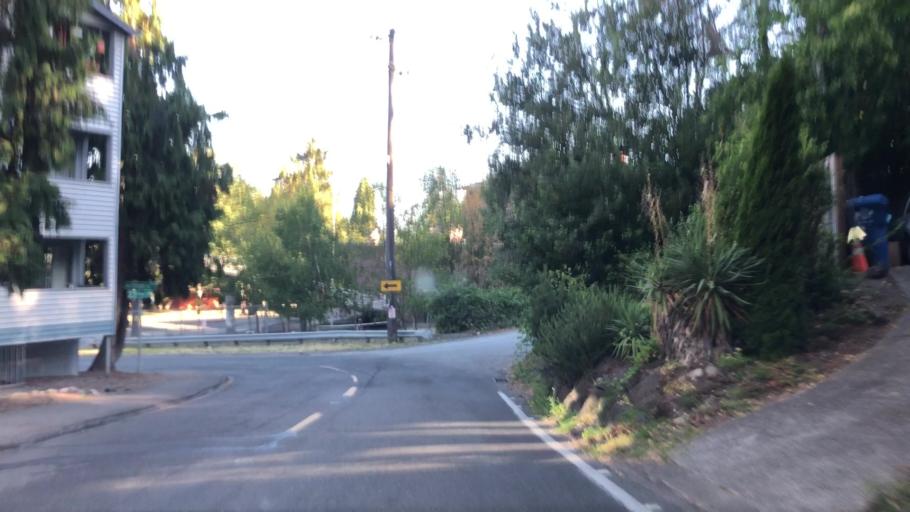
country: US
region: Washington
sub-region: King County
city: White Center
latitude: 47.5626
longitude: -122.3627
